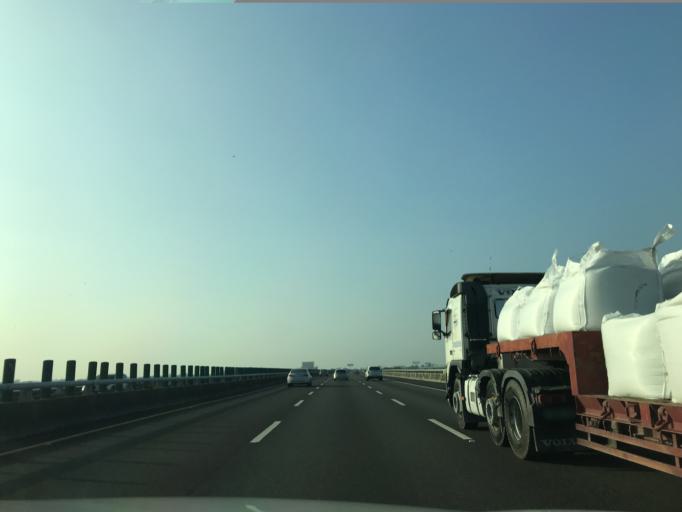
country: TW
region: Taiwan
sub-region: Yunlin
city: Douliu
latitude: 23.8078
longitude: 120.4839
